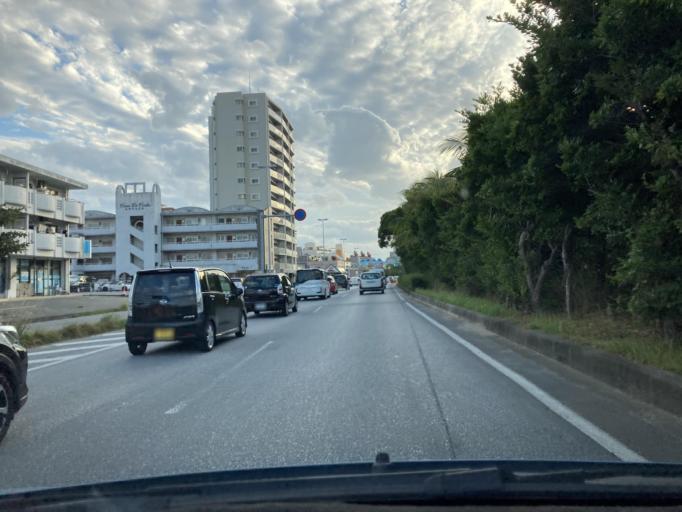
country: JP
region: Okinawa
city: Chatan
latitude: 26.2897
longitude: 127.7545
